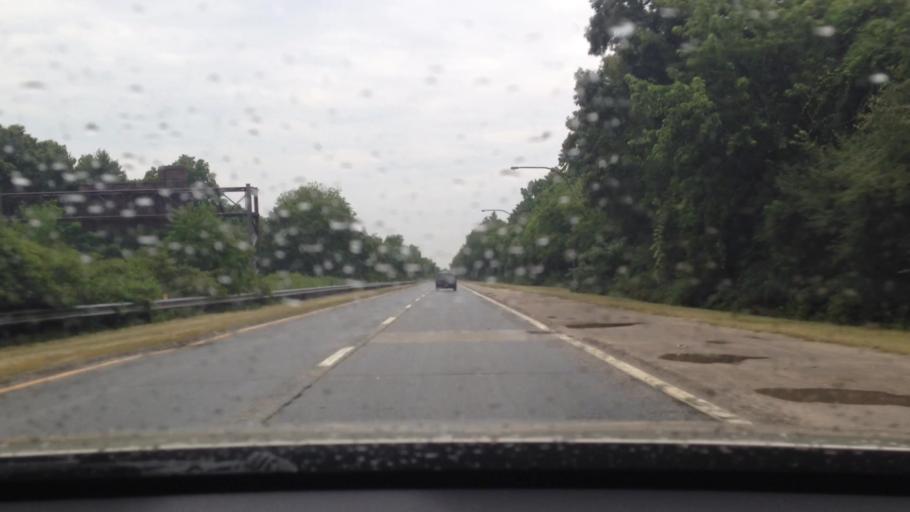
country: US
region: New York
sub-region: Suffolk County
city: Bay Wood
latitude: 40.7547
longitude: -73.2797
